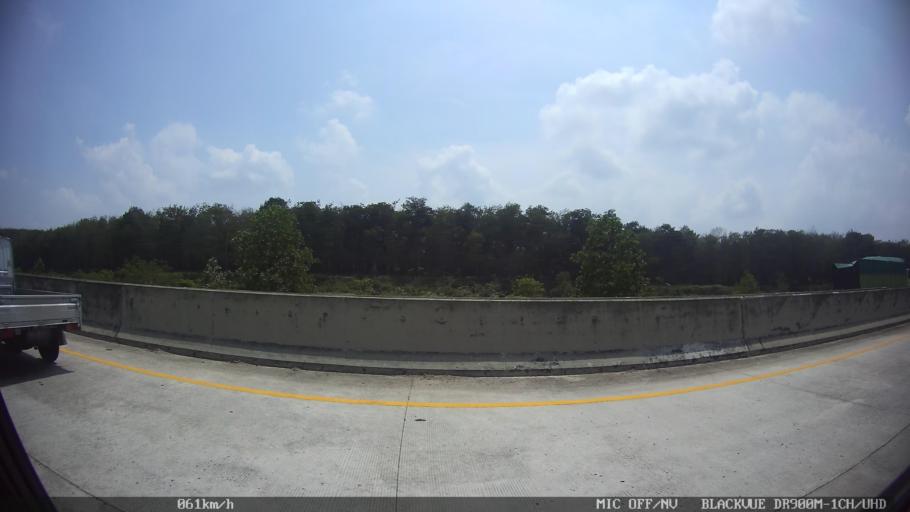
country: ID
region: Lampung
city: Kedaton
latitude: -5.3899
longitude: 105.3425
